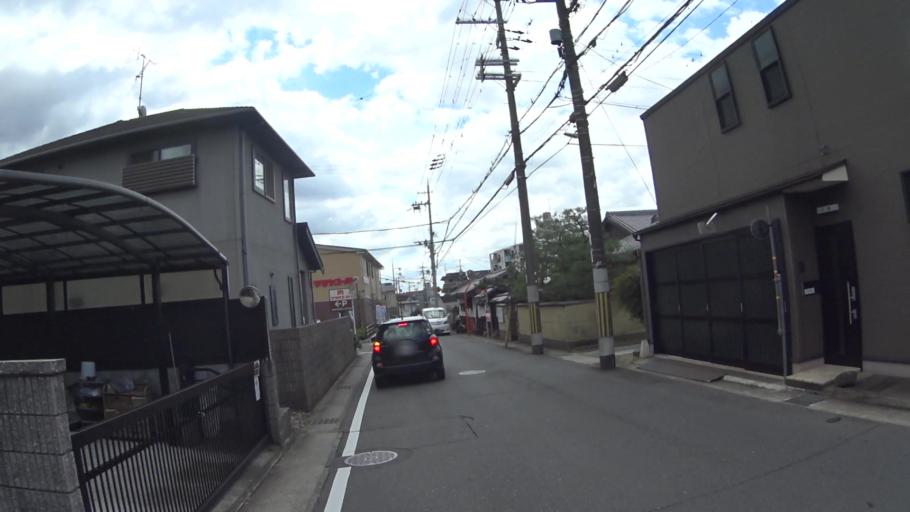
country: JP
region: Shiga Prefecture
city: Otsu-shi
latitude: 34.9766
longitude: 135.8234
